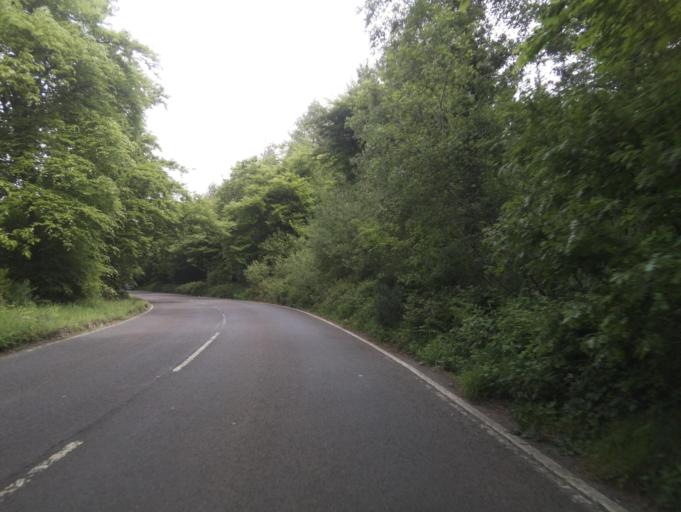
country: GB
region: England
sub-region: Devon
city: Exminster
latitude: 50.6420
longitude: -3.5424
